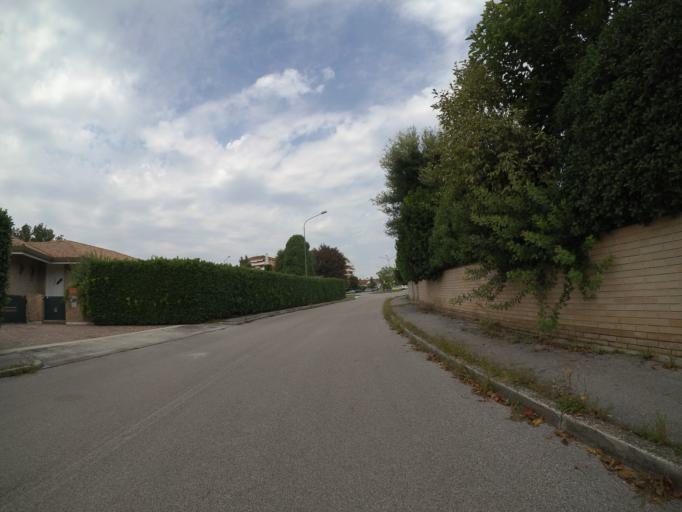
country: IT
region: Friuli Venezia Giulia
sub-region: Provincia di Udine
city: Codroipo
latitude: 45.9527
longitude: 12.9918
